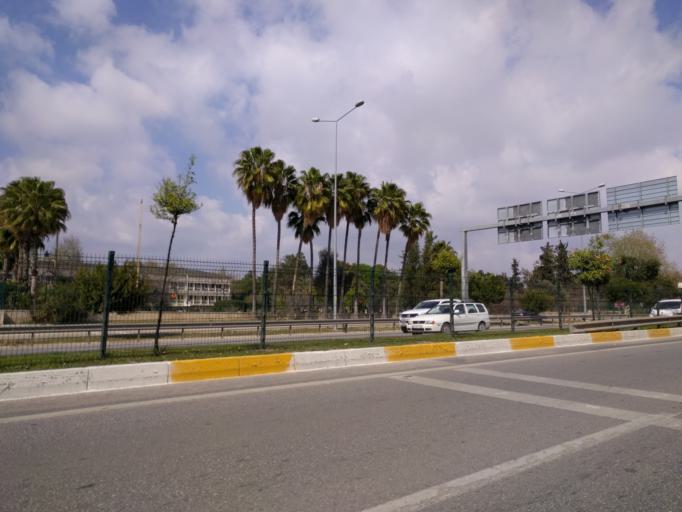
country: TR
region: Antalya
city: Antalya
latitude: 36.9022
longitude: 30.6691
